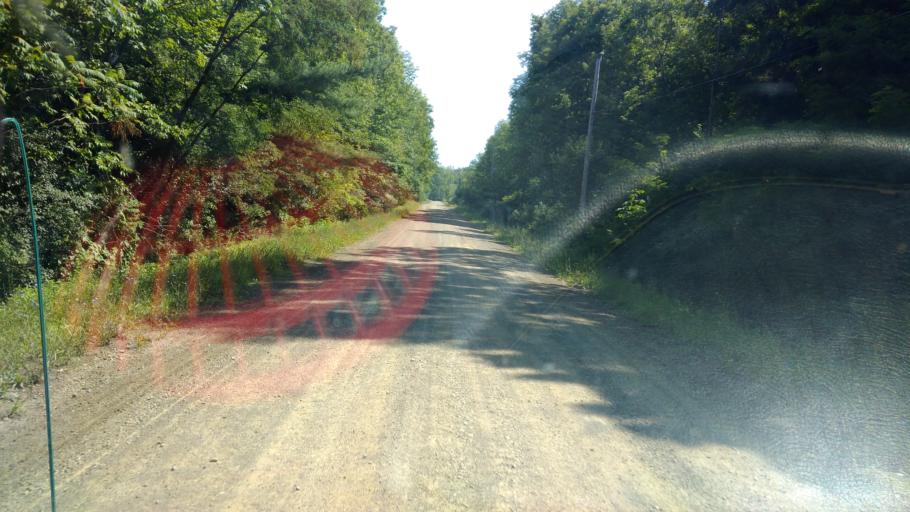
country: US
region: New York
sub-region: Allegany County
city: Houghton
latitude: 42.3640
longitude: -78.0465
